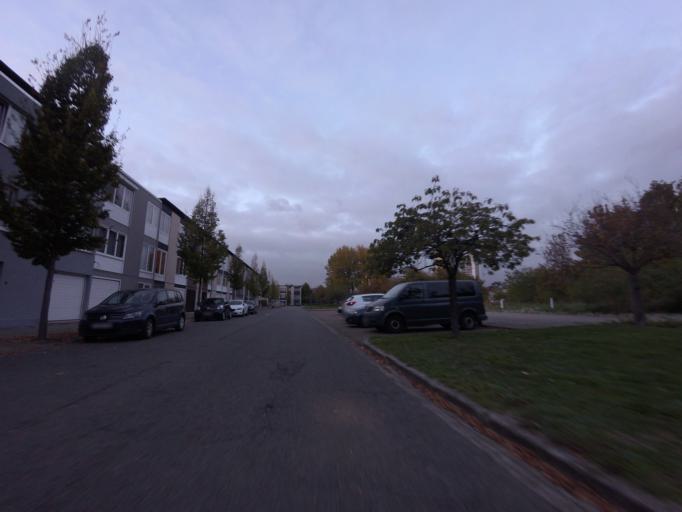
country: BE
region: Flanders
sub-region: Provincie Antwerpen
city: Antwerpen
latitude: 51.2296
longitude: 4.3819
